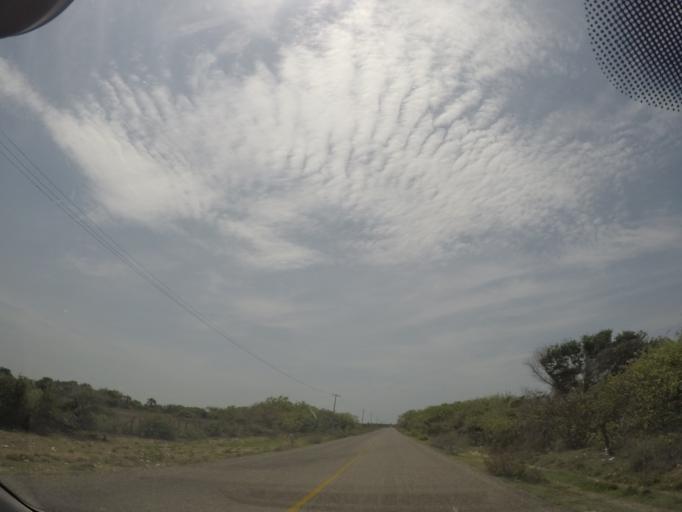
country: MX
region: Oaxaca
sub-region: San Mateo del Mar
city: Colonia Juarez
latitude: 16.2137
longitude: -95.0580
